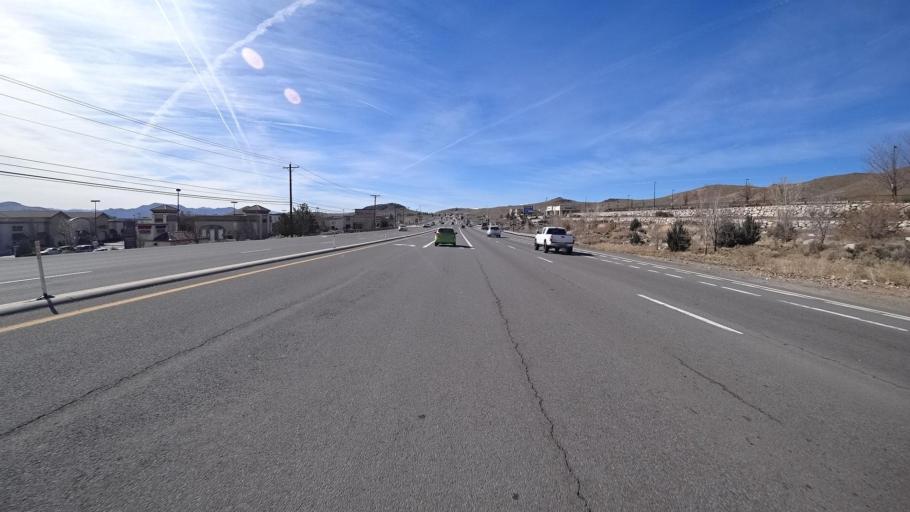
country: US
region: Nevada
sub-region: Washoe County
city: Sun Valley
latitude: 39.5854
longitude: -119.7424
